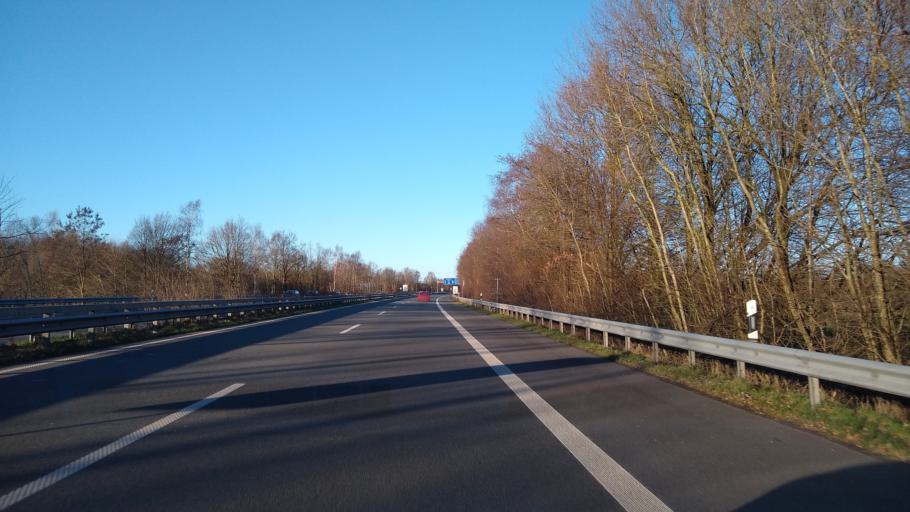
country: DE
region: Lower Saxony
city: Oldenburg
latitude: 53.1970
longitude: 8.2219
